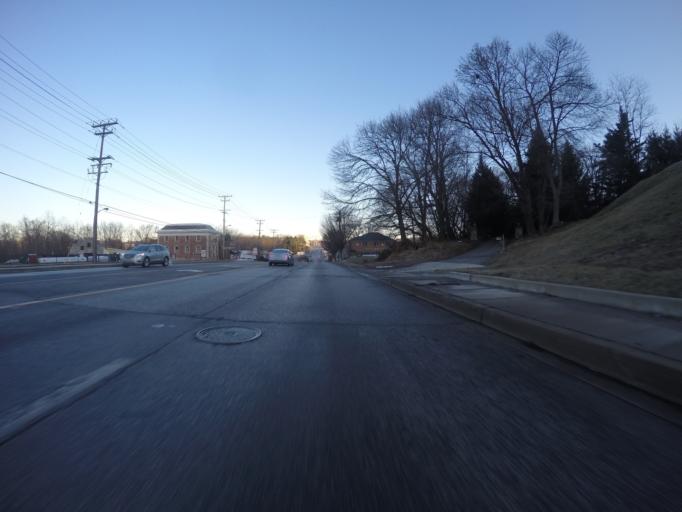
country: US
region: Maryland
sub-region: Baltimore County
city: Cockeysville
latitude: 39.4833
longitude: -76.6447
